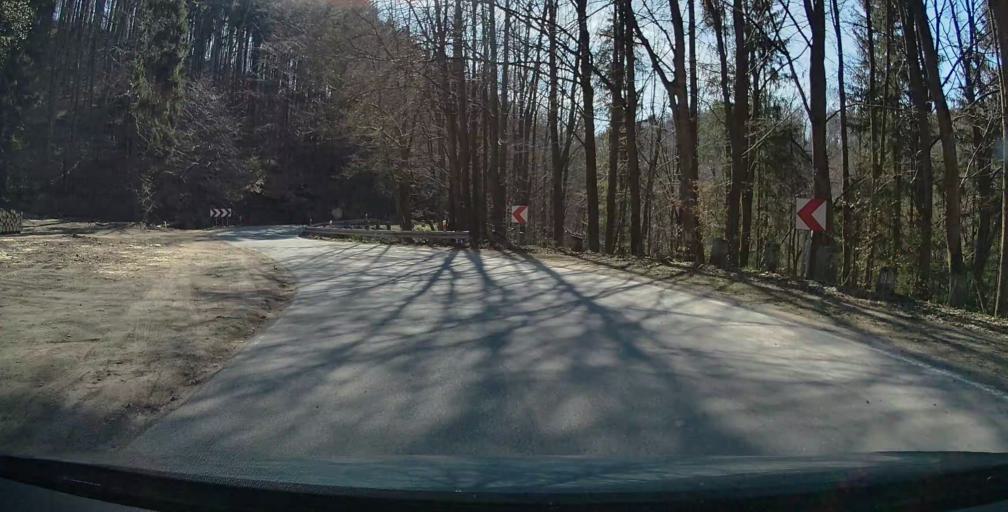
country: PL
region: Lower Silesian Voivodeship
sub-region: Powiat klodzki
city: Kudowa-Zdroj
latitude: 50.4516
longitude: 16.2826
